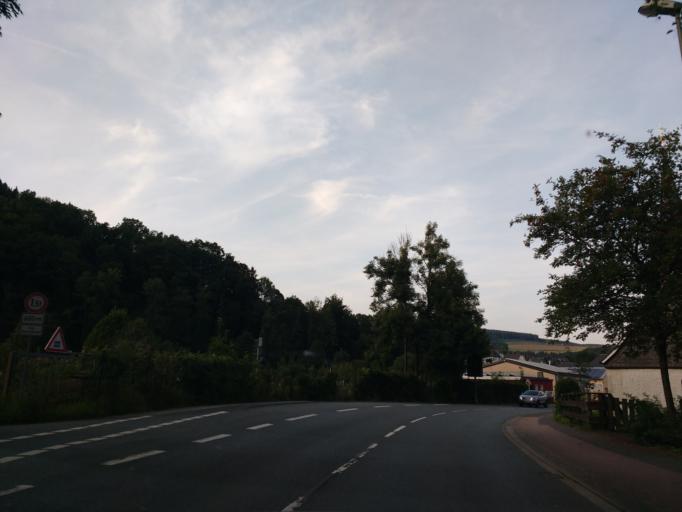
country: DE
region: North Rhine-Westphalia
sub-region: Regierungsbezirk Arnsberg
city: Bestwig
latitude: 51.3677
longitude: 8.4143
